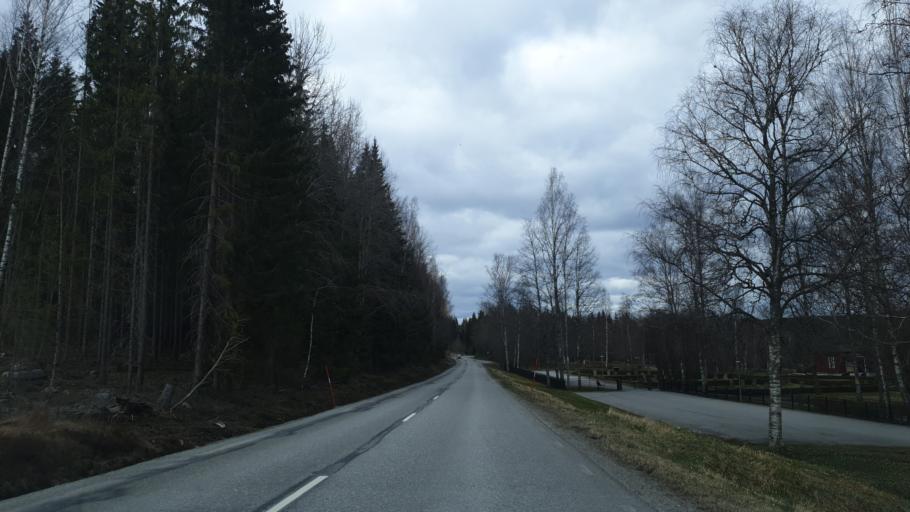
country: SE
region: OErebro
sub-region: Nora Kommun
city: Nora
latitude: 59.5432
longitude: 15.0301
